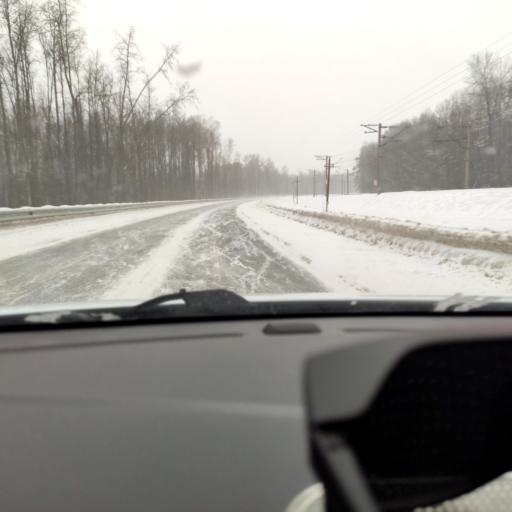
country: RU
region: Tatarstan
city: Vysokaya Gora
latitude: 55.9205
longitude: 49.2832
